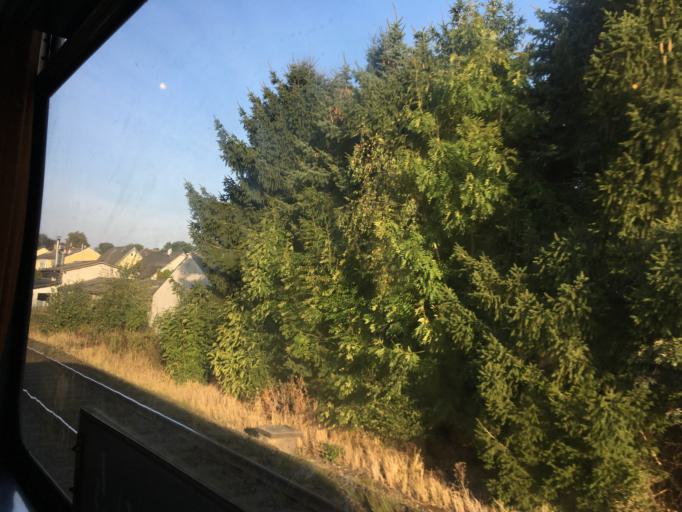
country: DE
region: North Rhine-Westphalia
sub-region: Regierungsbezirk Arnsberg
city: Unna
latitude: 51.4775
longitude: 7.6938
